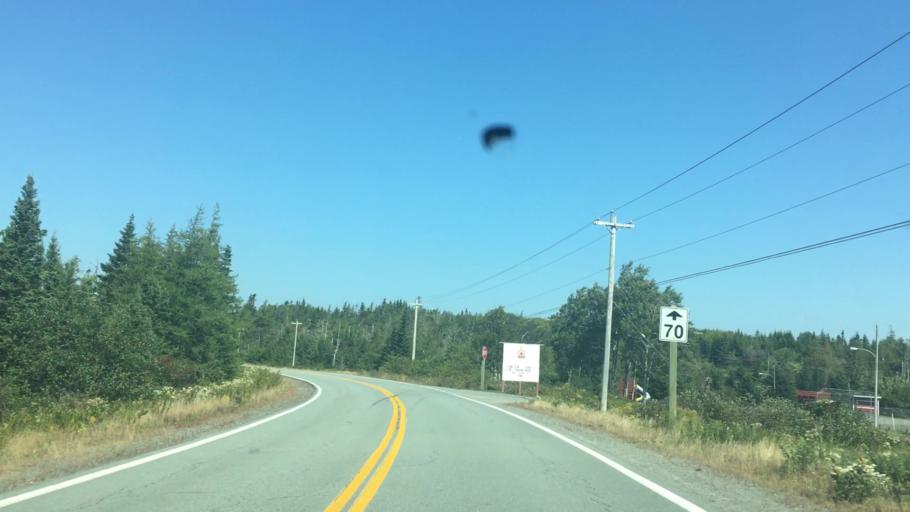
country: CA
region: Nova Scotia
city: Antigonish
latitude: 45.0213
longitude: -62.0312
